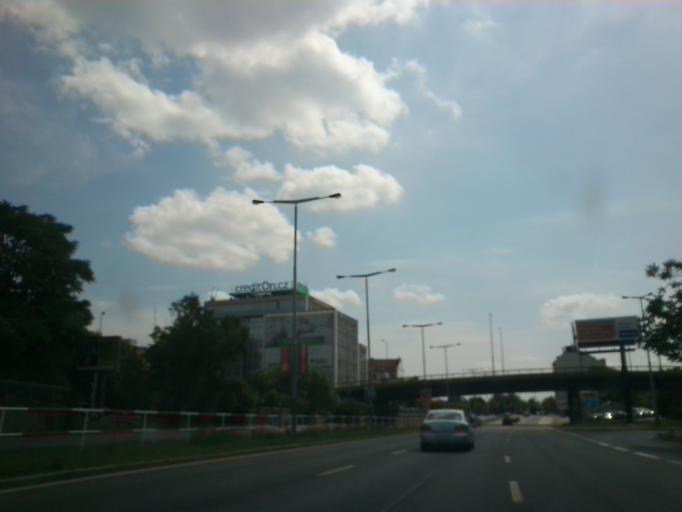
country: CZ
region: Praha
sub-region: Praha 8
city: Karlin
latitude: 50.1109
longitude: 14.4449
